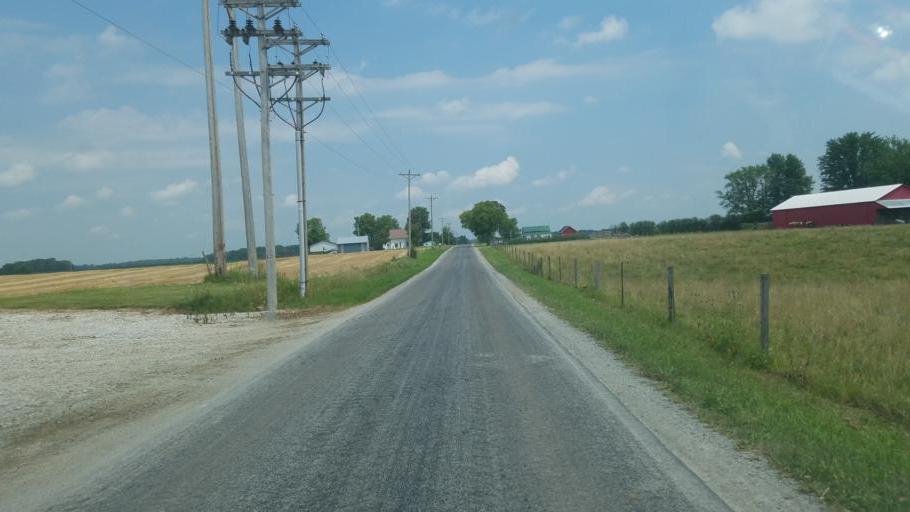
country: US
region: Ohio
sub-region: Hardin County
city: Kenton
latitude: 40.5859
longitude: -83.4526
